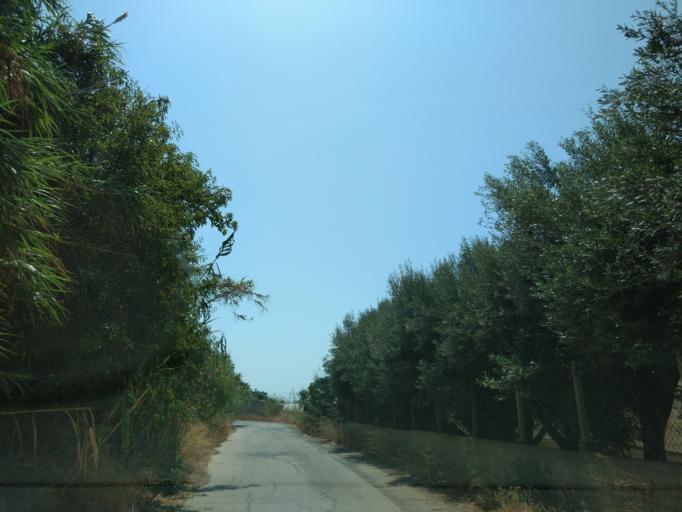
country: IT
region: Sicily
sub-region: Ragusa
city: Cava d'Aliga
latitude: 36.7322
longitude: 14.6979
